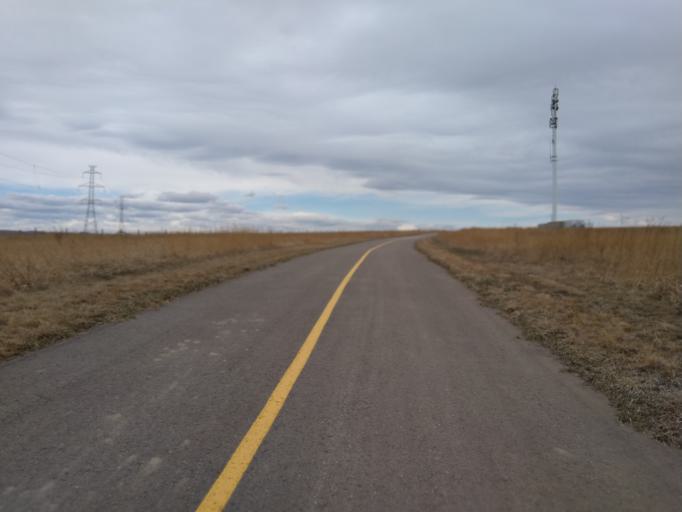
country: CA
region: Alberta
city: Calgary
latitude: 51.1745
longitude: -114.0638
